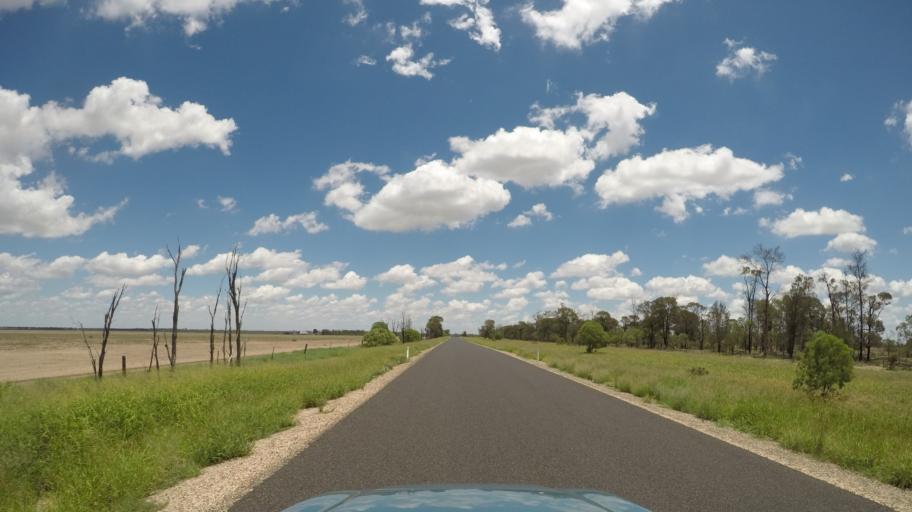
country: AU
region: Queensland
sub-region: Goondiwindi
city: Goondiwindi
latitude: -28.1619
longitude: 150.1440
